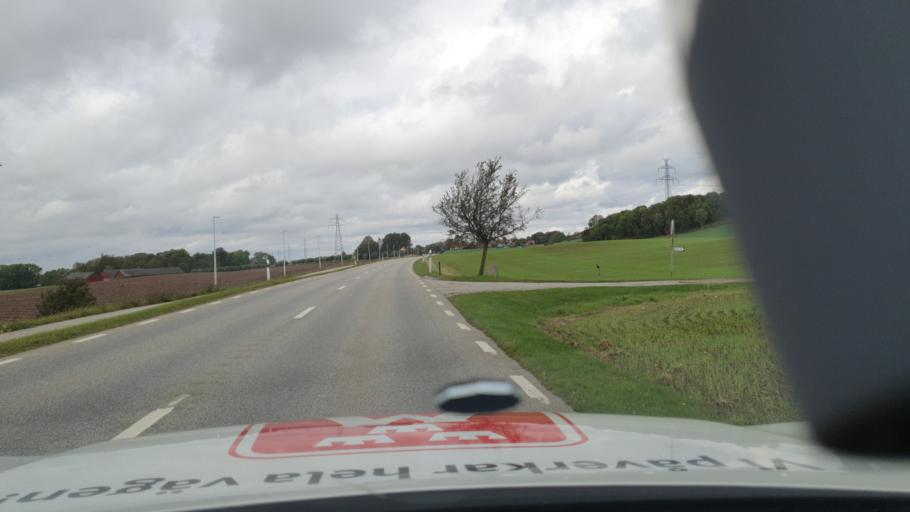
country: SE
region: Skane
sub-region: Malmo
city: Oxie
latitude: 55.5101
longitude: 13.0955
